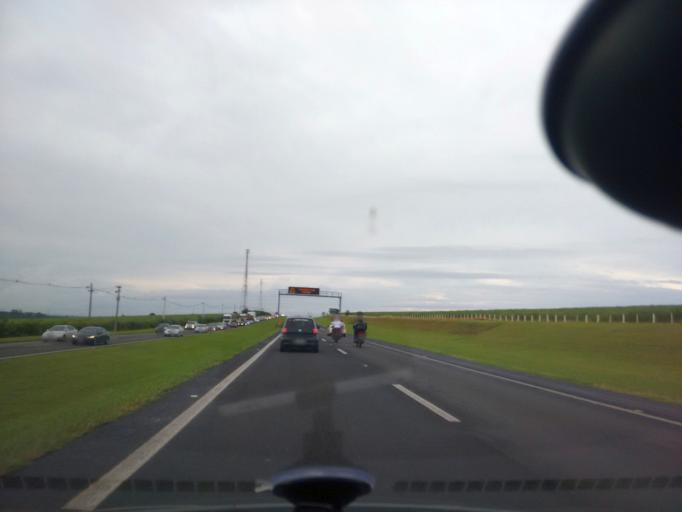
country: BR
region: Sao Paulo
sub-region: Itirapina
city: Itirapina
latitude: -22.1972
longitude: -47.7746
